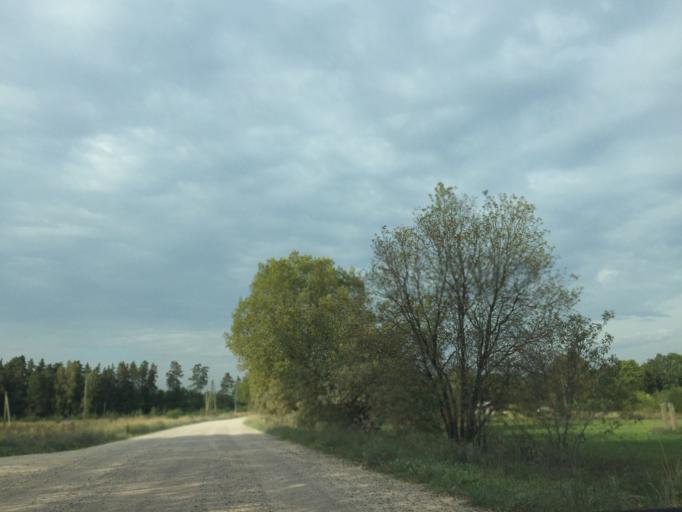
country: LV
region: Ikskile
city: Ikskile
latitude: 56.8111
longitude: 24.4475
